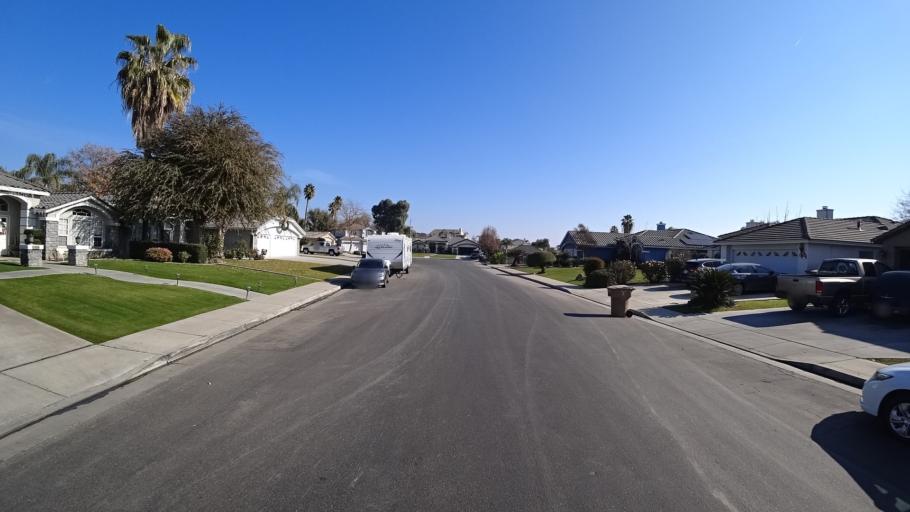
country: US
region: California
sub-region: Kern County
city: Greenacres
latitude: 35.3155
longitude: -119.1241
